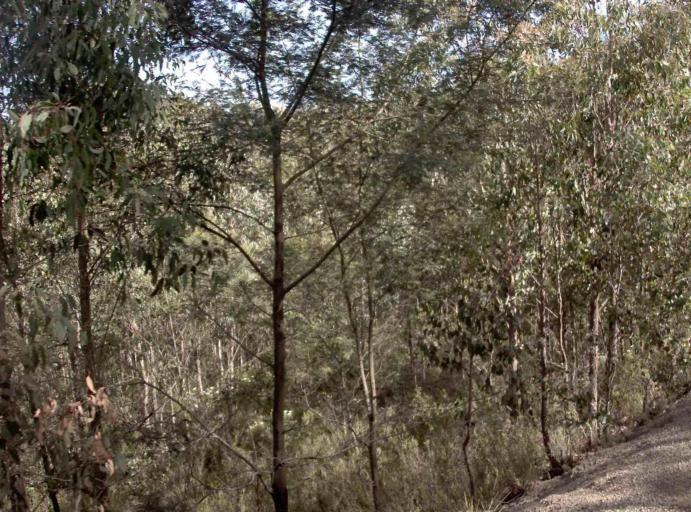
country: AU
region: Victoria
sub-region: East Gippsland
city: Lakes Entrance
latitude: -37.4762
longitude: 148.1245
